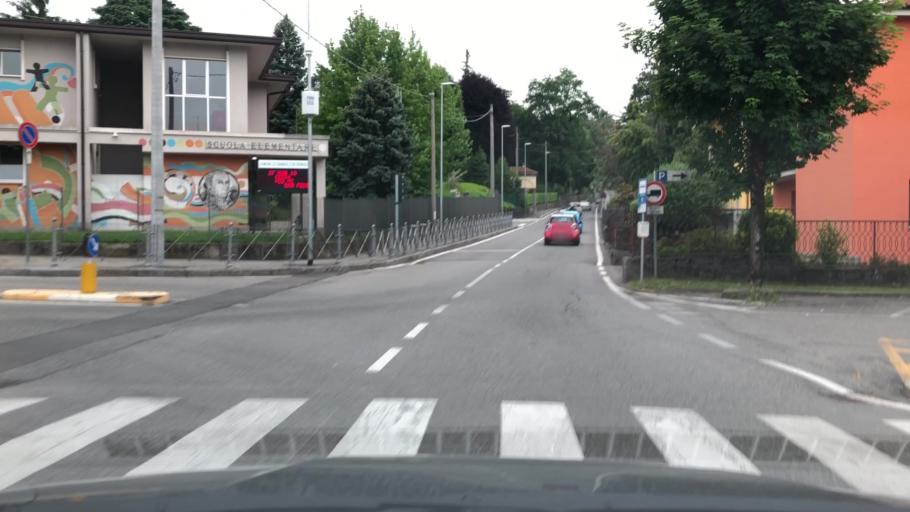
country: IT
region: Lombardy
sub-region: Provincia di Como
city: Casnate Con Bernate
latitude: 45.7610
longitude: 9.0756
